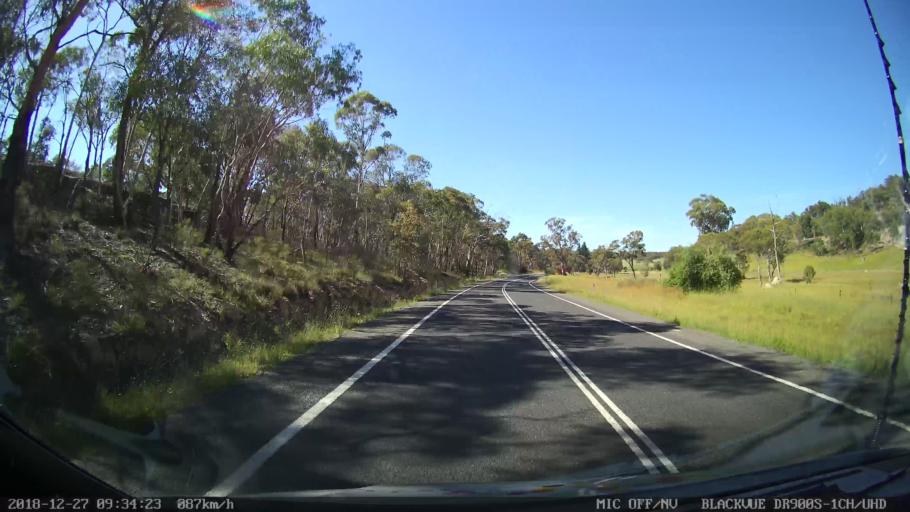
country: AU
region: New South Wales
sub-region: Lithgow
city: Portland
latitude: -33.2255
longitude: 150.0278
